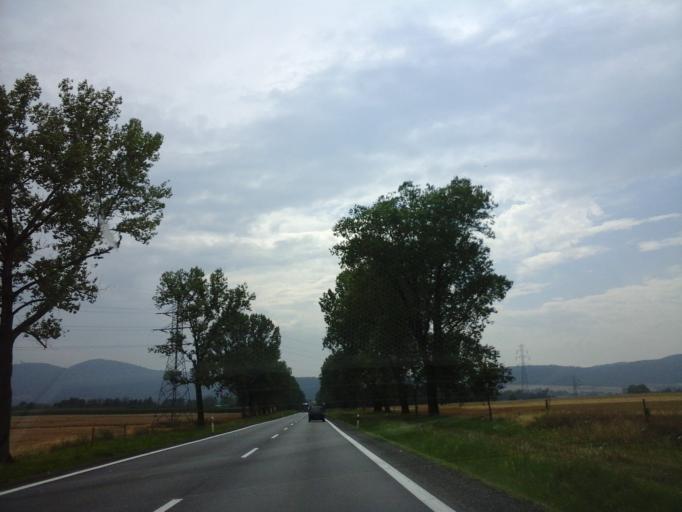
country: PL
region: Lower Silesian Voivodeship
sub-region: Powiat zabkowicki
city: Bardo
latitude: 50.5346
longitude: 16.7843
